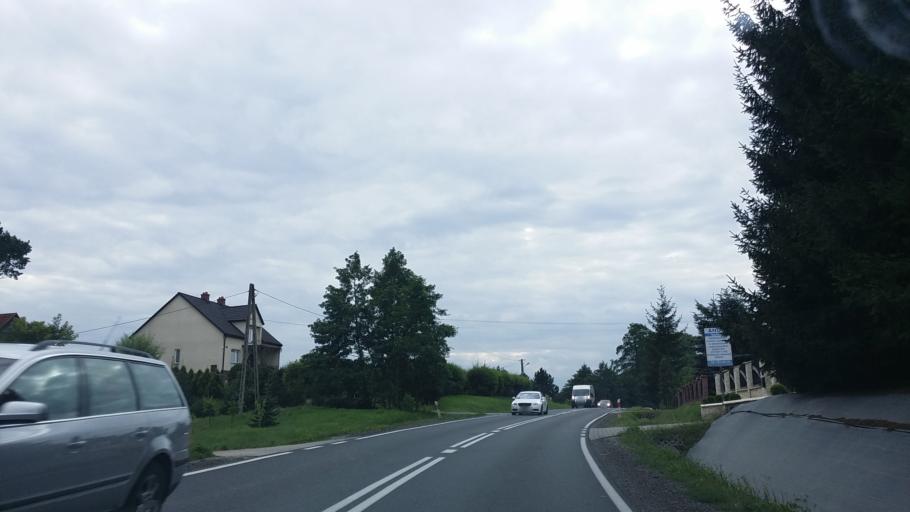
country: PL
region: Lesser Poland Voivodeship
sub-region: Powiat wadowicki
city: Sosnowice
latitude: 49.9576
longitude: 19.7150
